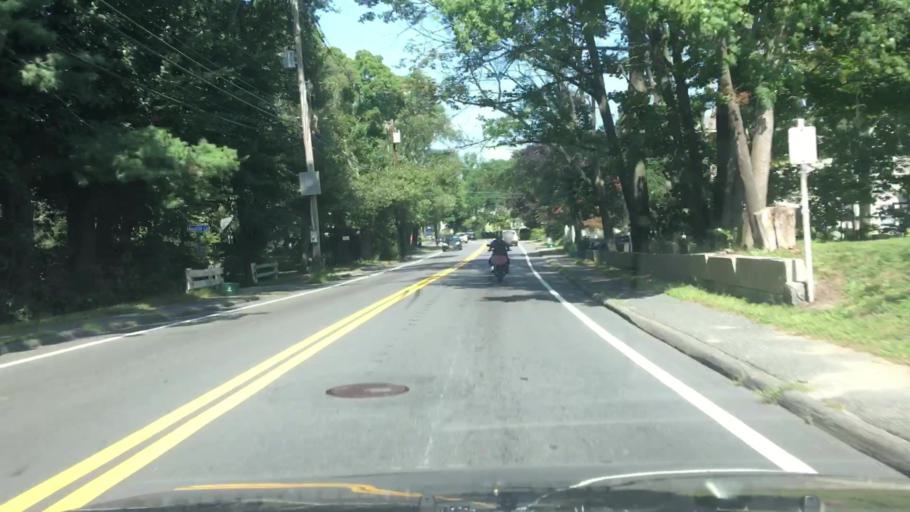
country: US
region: Massachusetts
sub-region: Middlesex County
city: Holliston
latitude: 42.1963
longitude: -71.4332
